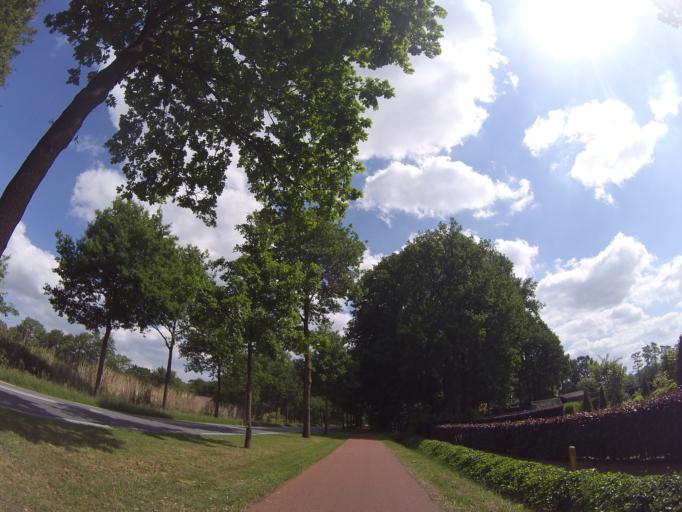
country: NL
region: Gelderland
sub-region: Gemeente Barneveld
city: Barneveld
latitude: 52.1725
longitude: 5.5621
